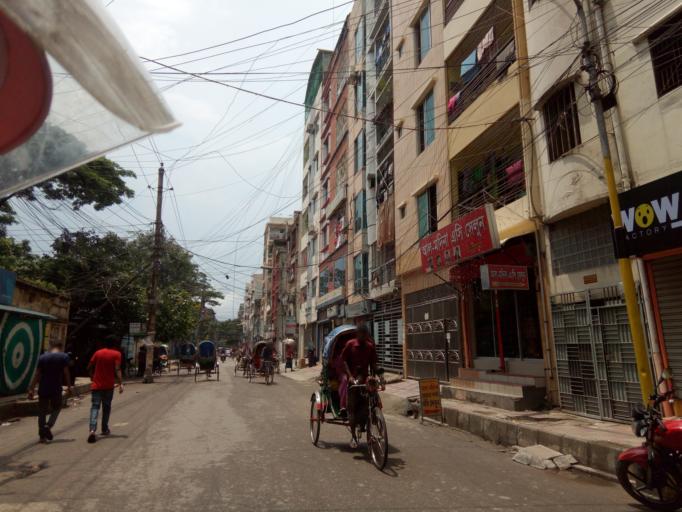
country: BD
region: Dhaka
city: Azimpur
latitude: 23.7603
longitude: 90.3637
